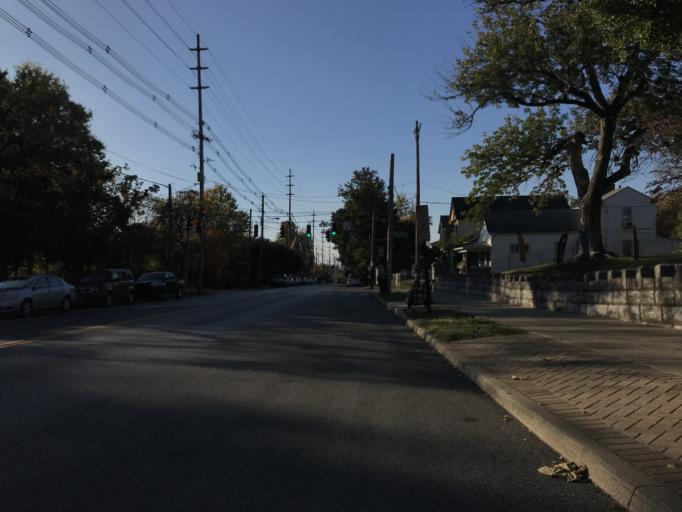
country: US
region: Indiana
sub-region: Clark County
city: Jeffersonville
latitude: 38.2563
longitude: -85.7149
